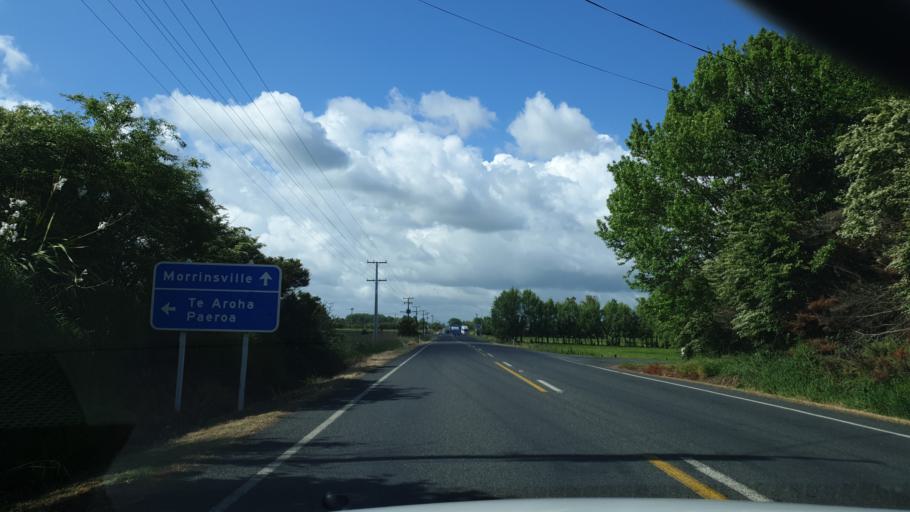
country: NZ
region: Waikato
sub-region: Hauraki District
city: Paeroa
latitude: -37.5124
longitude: 175.4966
